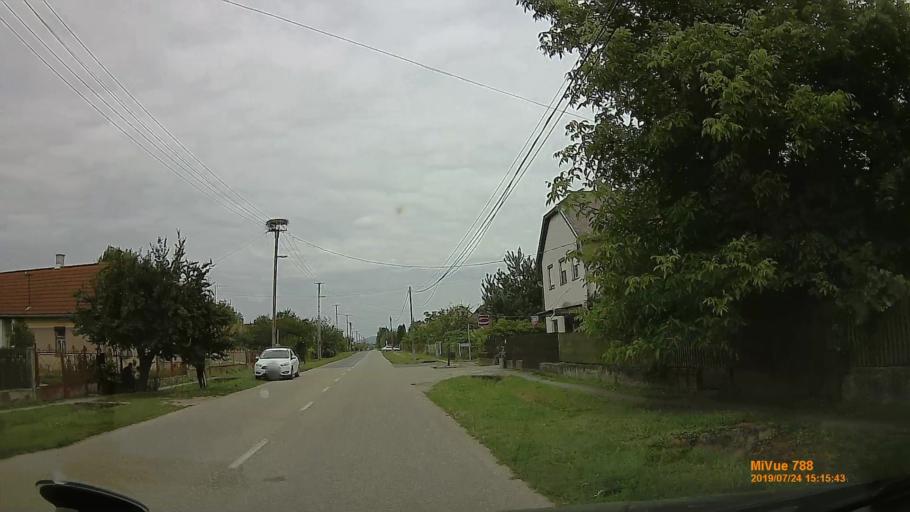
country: HU
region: Szabolcs-Szatmar-Bereg
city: Tarpa
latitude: 48.1972
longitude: 22.5343
